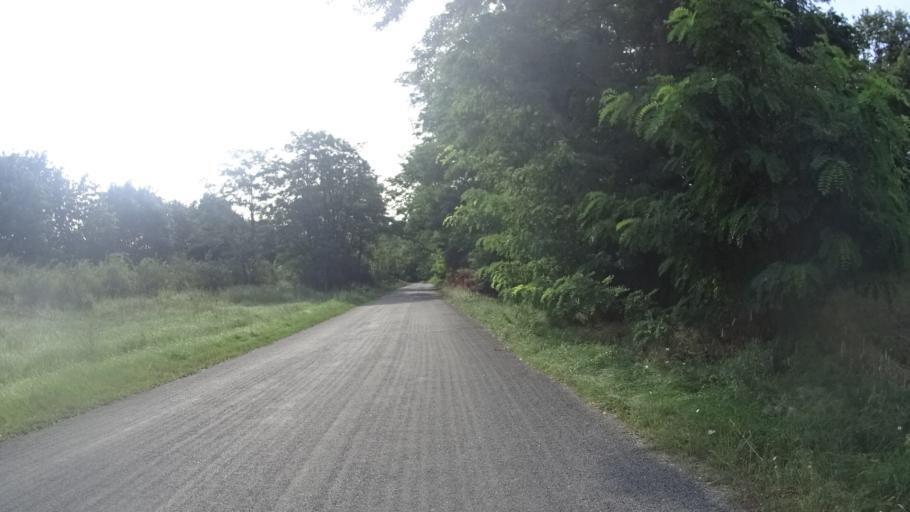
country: DE
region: Brandenburg
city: Golzow
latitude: 52.3270
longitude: 12.6721
